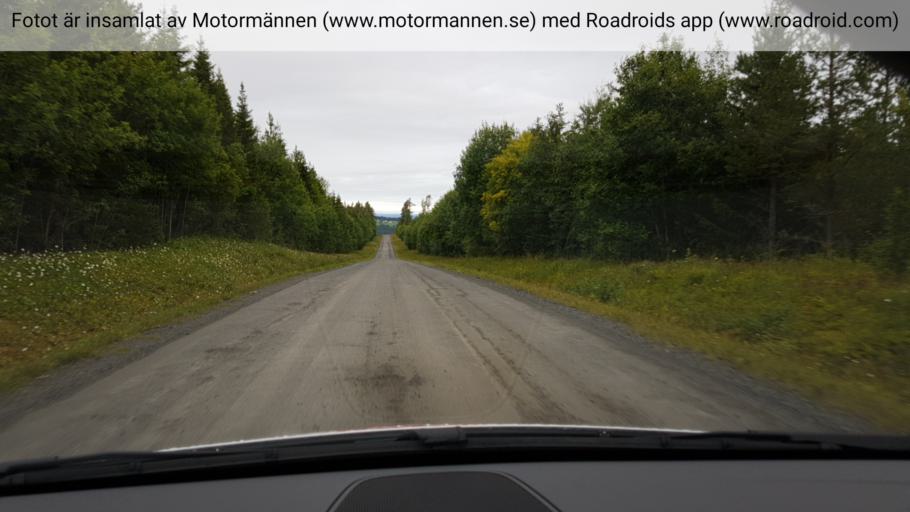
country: SE
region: Jaemtland
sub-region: OEstersunds Kommun
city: Lit
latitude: 63.6784
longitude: 14.8168
